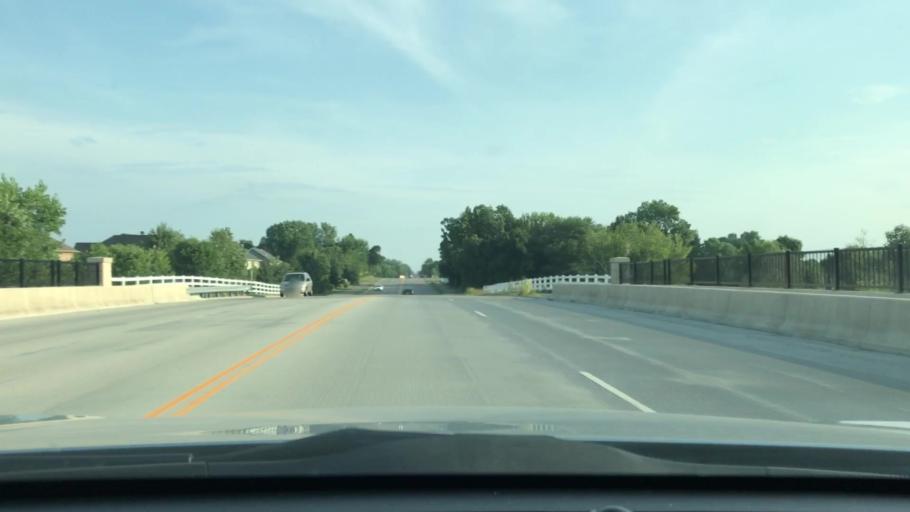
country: US
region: Minnesota
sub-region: Hennepin County
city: Maple Grove
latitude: 45.0501
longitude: -93.4818
